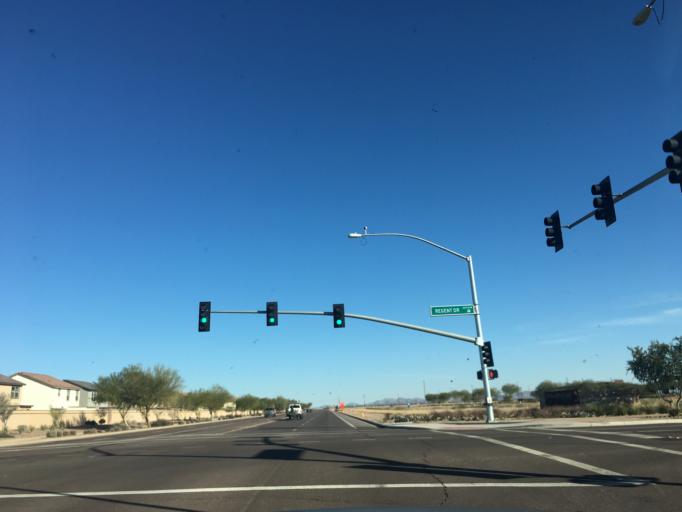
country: US
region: Arizona
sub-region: Pinal County
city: Maricopa
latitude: 33.0436
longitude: -112.0052
